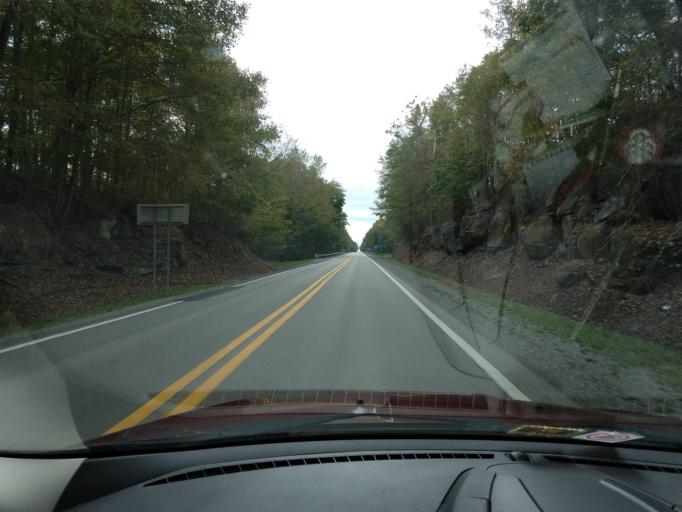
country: US
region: West Virginia
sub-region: Barbour County
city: Philippi
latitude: 39.1264
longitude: -79.9973
